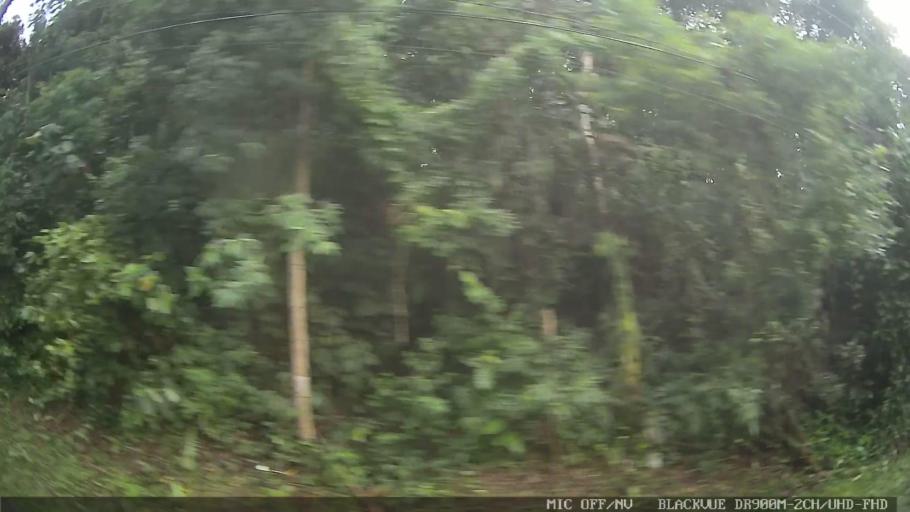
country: BR
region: Sao Paulo
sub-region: Rio Grande Da Serra
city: Rio Grande da Serra
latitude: -23.7084
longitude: -46.3523
